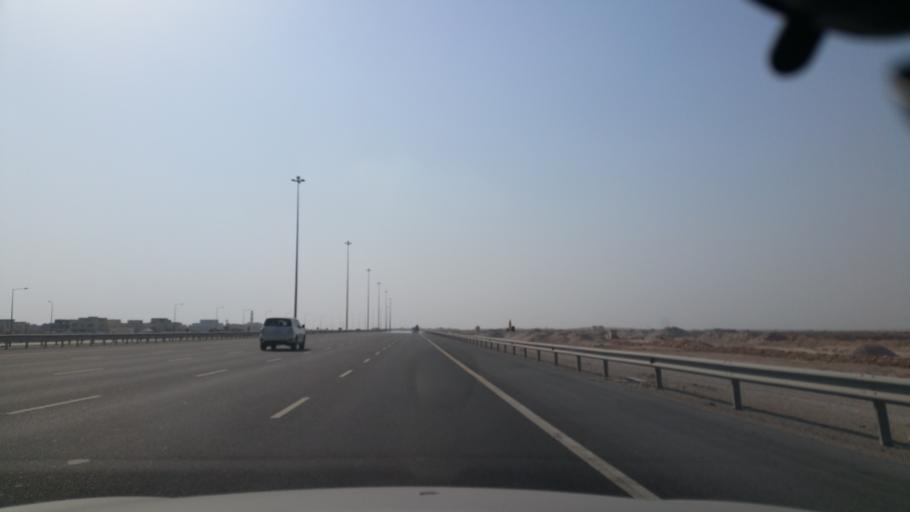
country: QA
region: Baladiyat Umm Salal
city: Umm Salal `Ali
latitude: 25.4572
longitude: 51.4541
